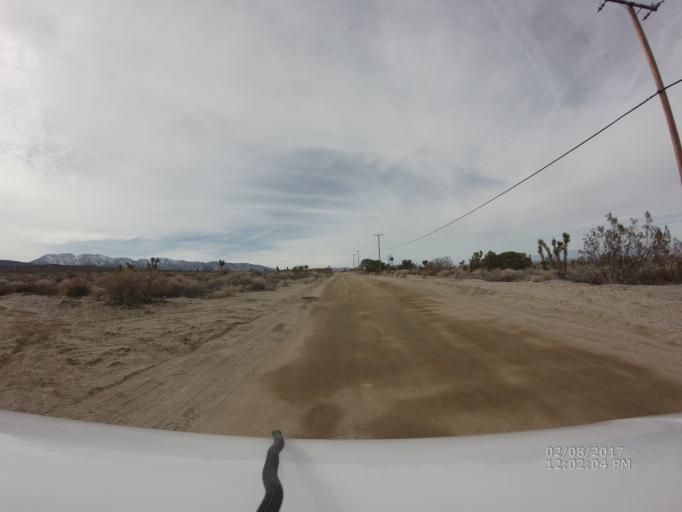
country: US
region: California
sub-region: San Bernardino County
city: Pinon Hills
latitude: 34.4695
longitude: -117.7653
